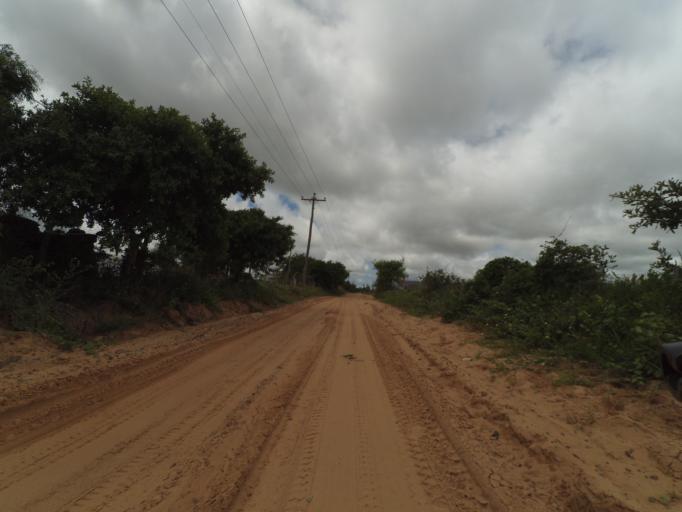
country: BO
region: Santa Cruz
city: Santa Rita
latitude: -17.9102
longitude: -63.2485
